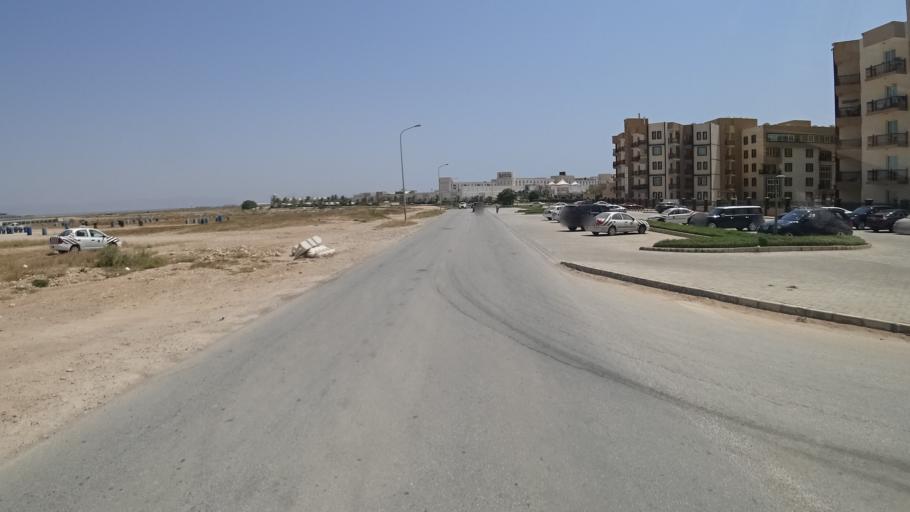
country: OM
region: Zufar
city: Salalah
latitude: 17.0241
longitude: 54.0604
